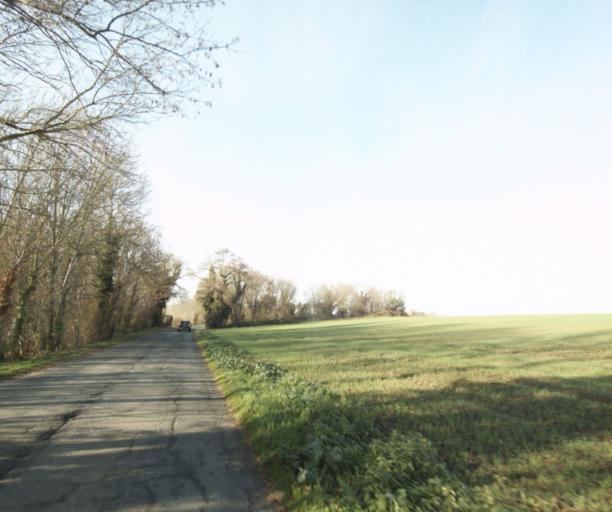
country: FR
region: Poitou-Charentes
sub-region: Departement de la Charente-Maritime
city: Chaniers
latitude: 45.7103
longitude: -0.5404
